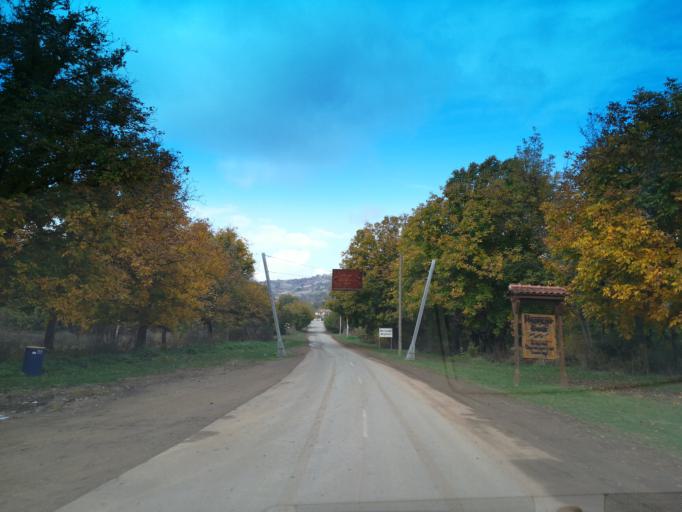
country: BG
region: Stara Zagora
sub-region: Obshtina Nikolaevo
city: Elkhovo
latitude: 42.3387
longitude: 25.4062
